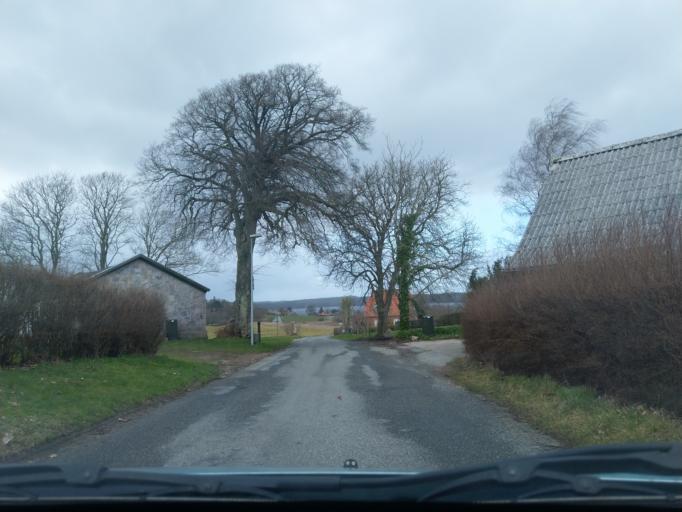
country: DK
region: Zealand
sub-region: Naestved Kommune
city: Fuglebjerg
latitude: 55.3544
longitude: 11.5761
